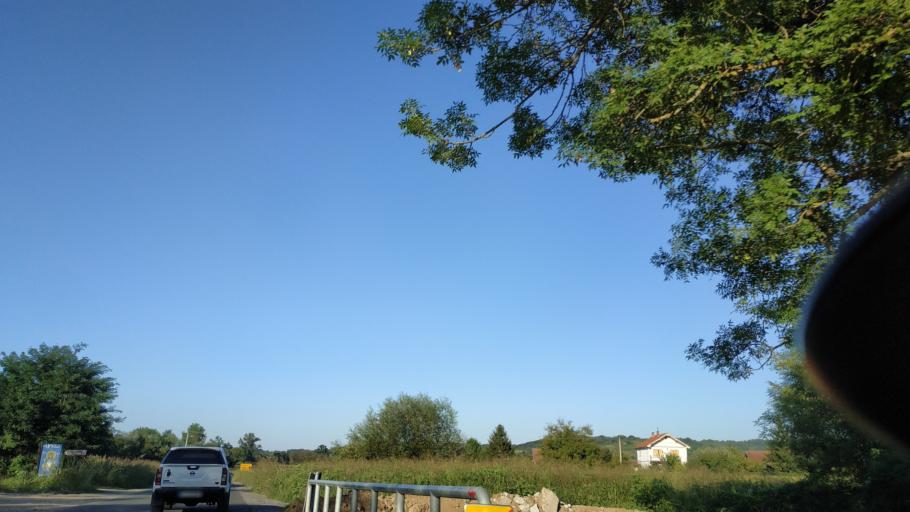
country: RS
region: Central Serbia
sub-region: Rasinski Okrug
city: Krusevac
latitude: 43.5260
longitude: 21.3368
